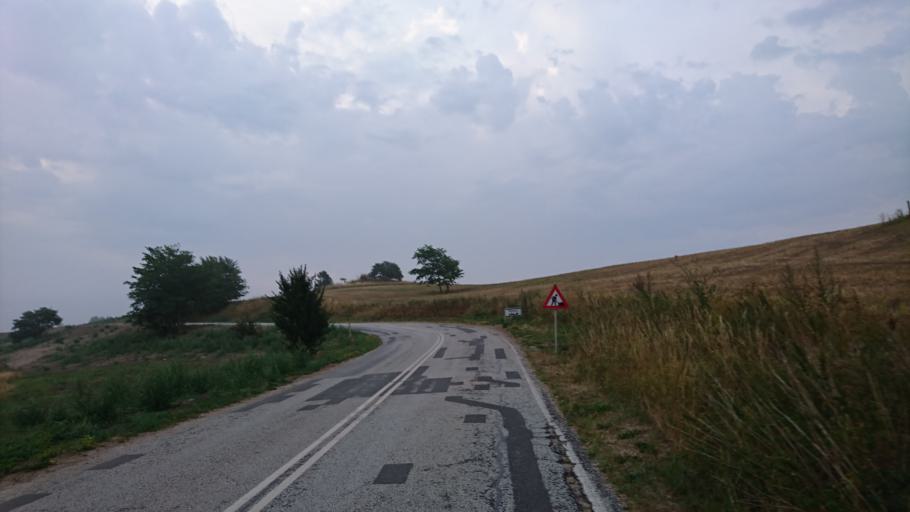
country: DK
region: Capital Region
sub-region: Egedal Kommune
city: Smorumnedre
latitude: 55.7574
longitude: 12.3053
